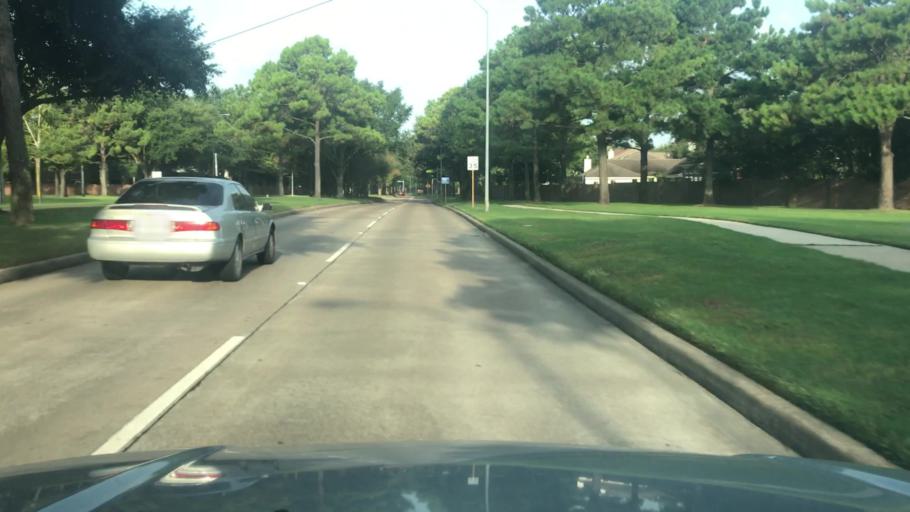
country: US
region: Texas
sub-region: Fort Bend County
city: Cinco Ranch
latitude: 29.7576
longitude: -95.7697
